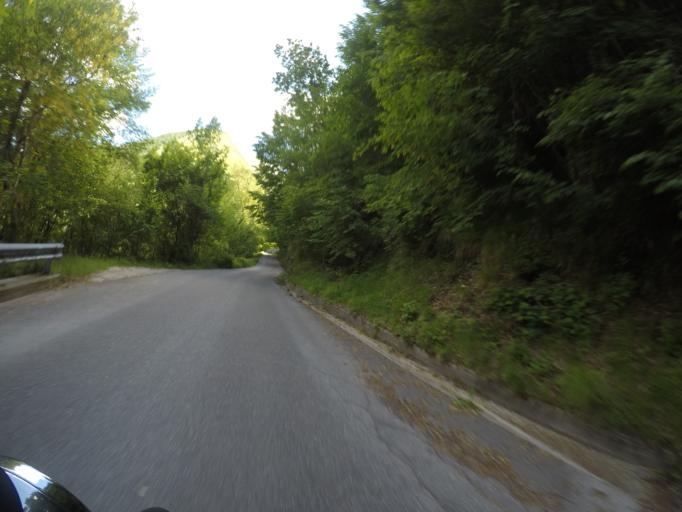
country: IT
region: Tuscany
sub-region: Provincia di Lucca
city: Minucciano
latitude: 44.1555
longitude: 10.1995
